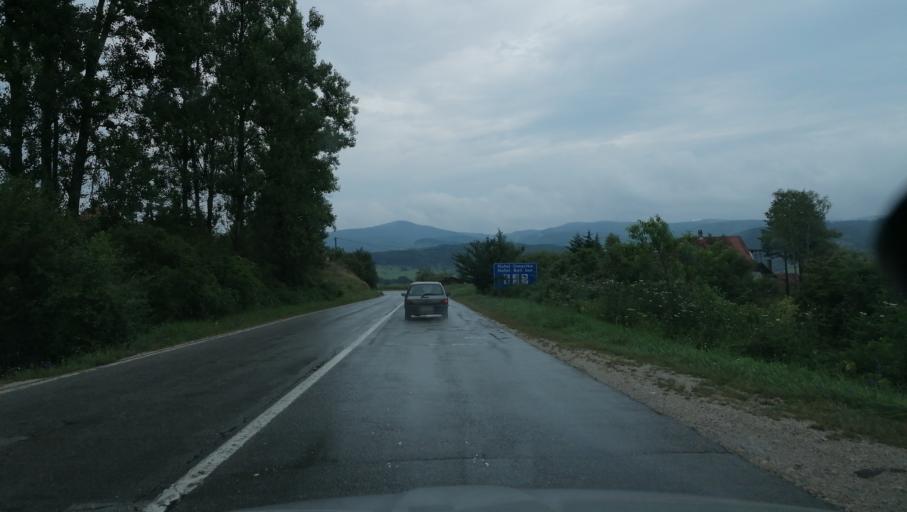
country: RS
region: Central Serbia
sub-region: Zlatiborski Okrug
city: Bajina Basta
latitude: 43.8457
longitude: 19.5926
